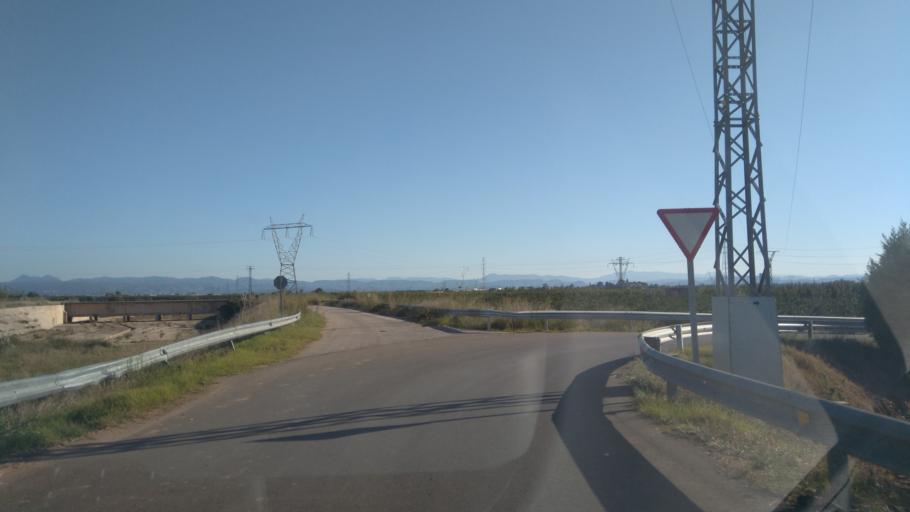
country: ES
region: Valencia
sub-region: Provincia de Valencia
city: L'Alcudia
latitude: 39.1888
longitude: -0.5199
